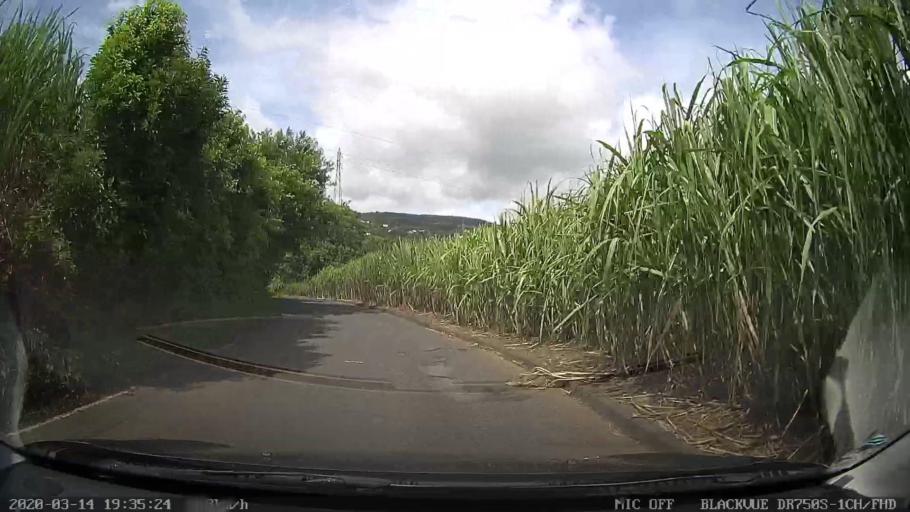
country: RE
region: Reunion
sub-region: Reunion
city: Sainte-Marie
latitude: -20.9376
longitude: 55.5230
